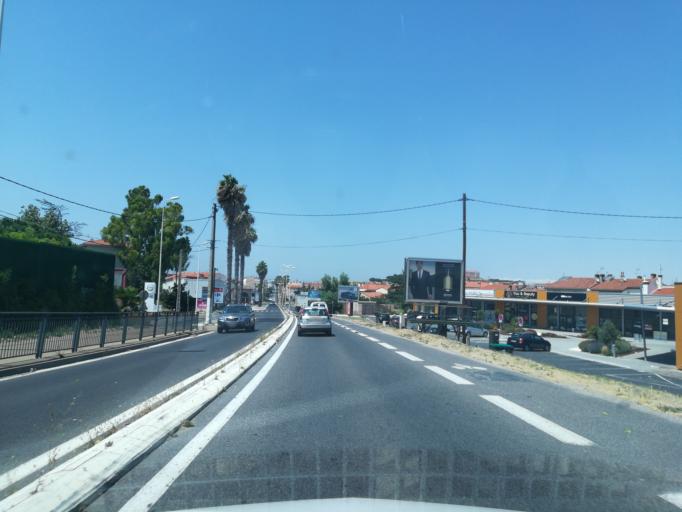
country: FR
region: Languedoc-Roussillon
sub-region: Departement des Pyrenees-Orientales
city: Perpignan
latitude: 42.6861
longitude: 2.8962
